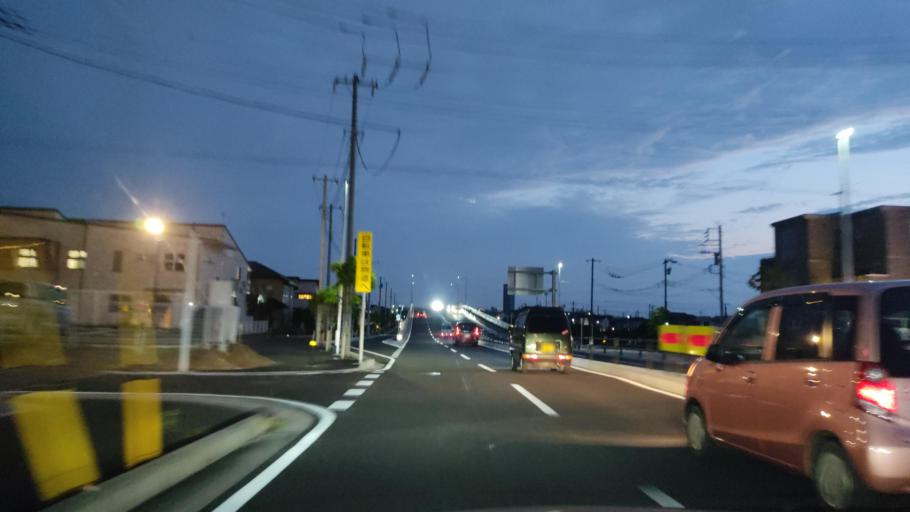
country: JP
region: Chiba
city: Nagareyama
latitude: 35.8471
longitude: 139.9080
